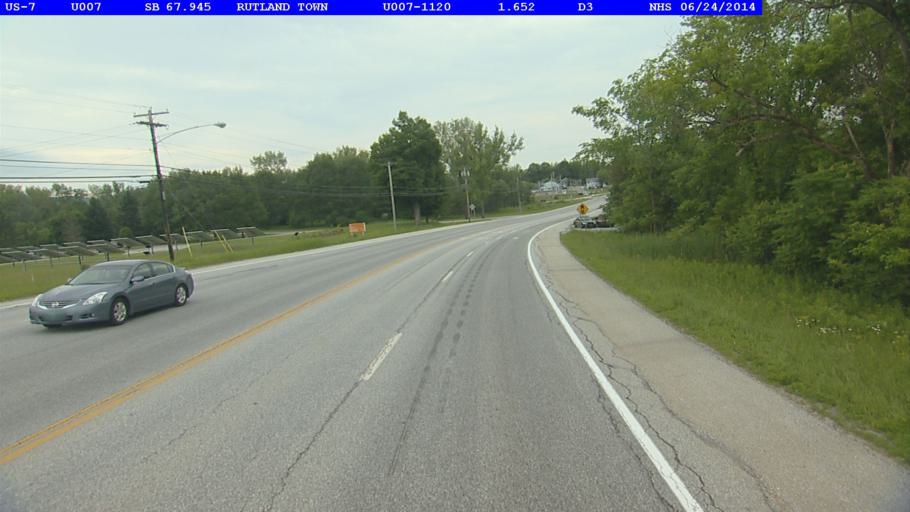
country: US
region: Vermont
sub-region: Rutland County
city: Rutland
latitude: 43.6374
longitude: -72.9758
